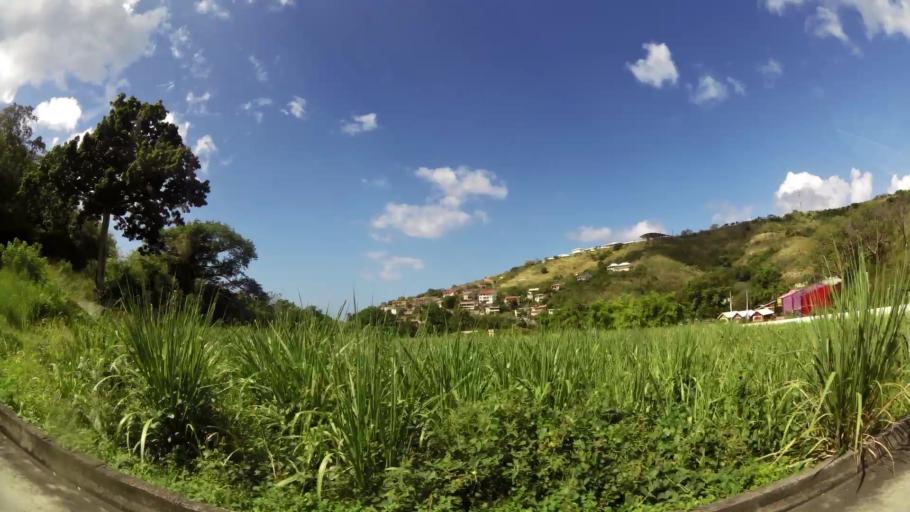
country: MQ
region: Martinique
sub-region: Martinique
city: Saint-Pierre
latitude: 14.6987
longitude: -61.1757
